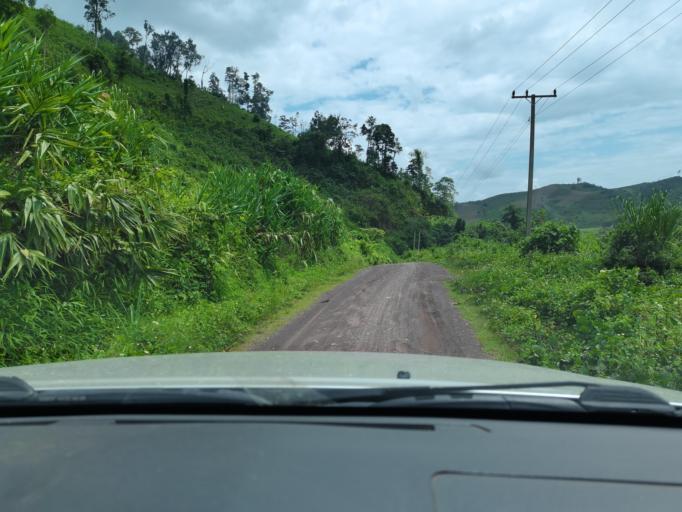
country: LA
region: Loungnamtha
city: Muang Long
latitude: 20.7124
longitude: 101.0129
